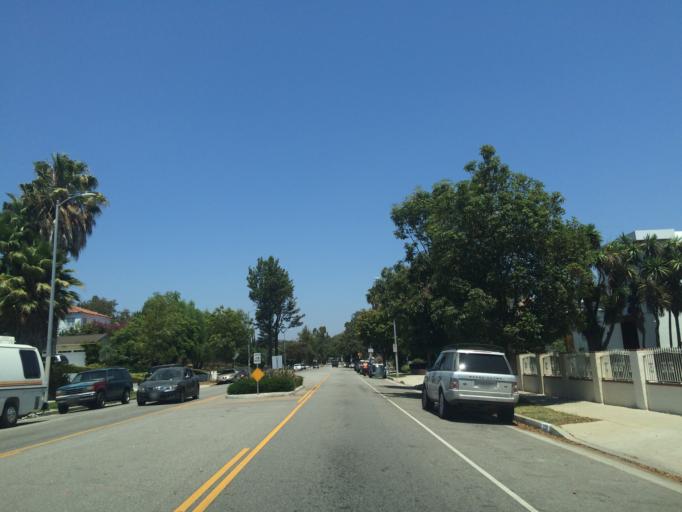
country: US
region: California
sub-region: Los Angeles County
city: Culver City
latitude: 34.0336
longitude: -118.3989
